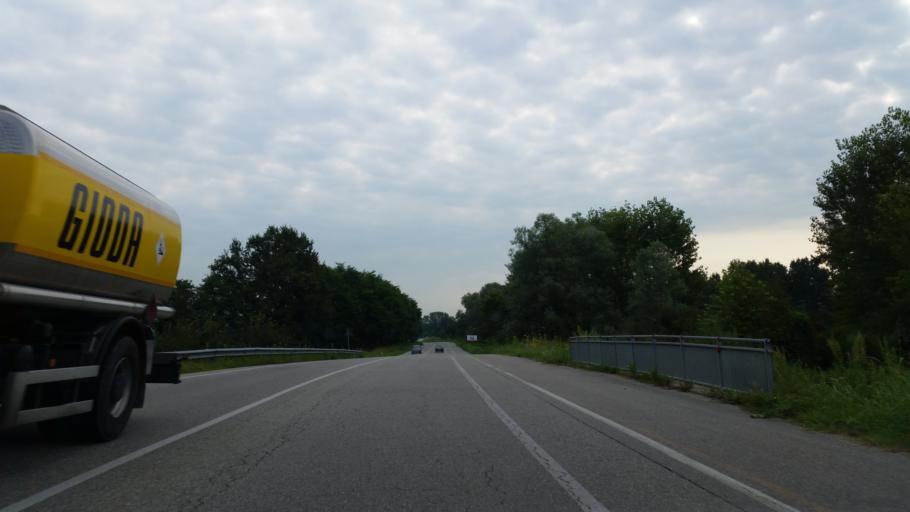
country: IT
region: Piedmont
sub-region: Provincia di Torino
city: San Sebastiano da Po
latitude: 45.1789
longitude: 7.9496
